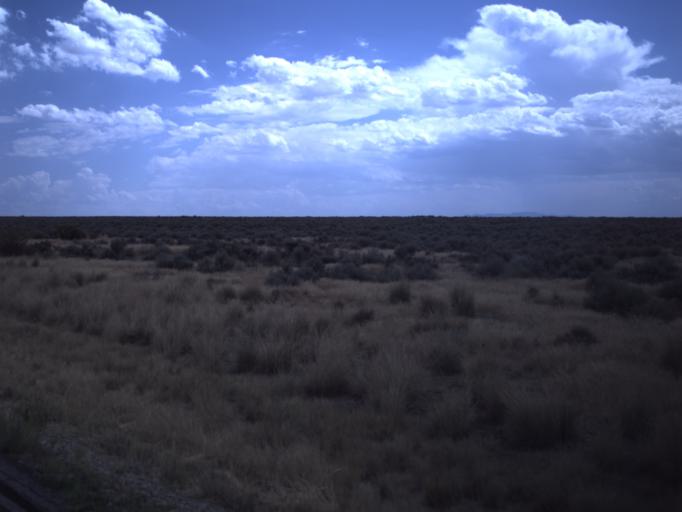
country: US
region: Utah
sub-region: Tooele County
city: Tooele
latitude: 40.3659
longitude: -112.3434
